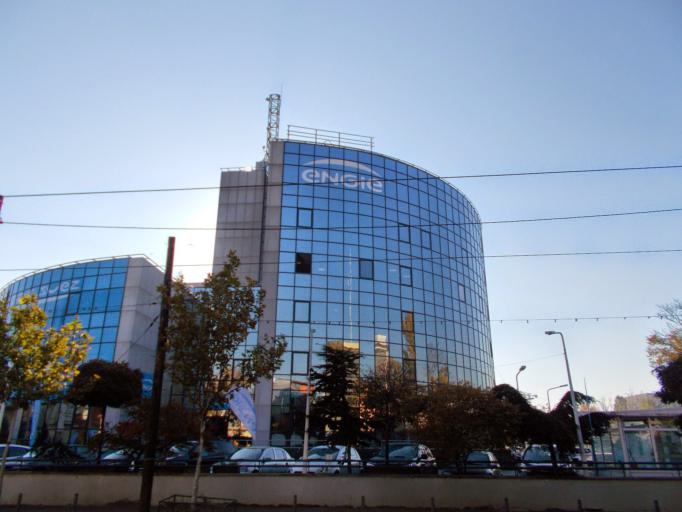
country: RO
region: Bucuresti
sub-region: Municipiul Bucuresti
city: Bucuresti
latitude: 44.4191
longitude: 26.0978
